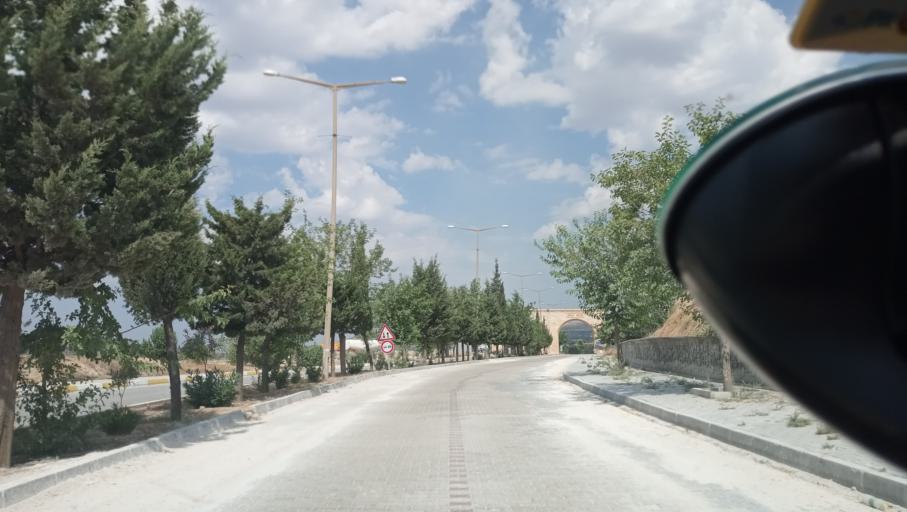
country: TR
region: Mardin
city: Kabala
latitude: 37.3425
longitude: 40.8066
